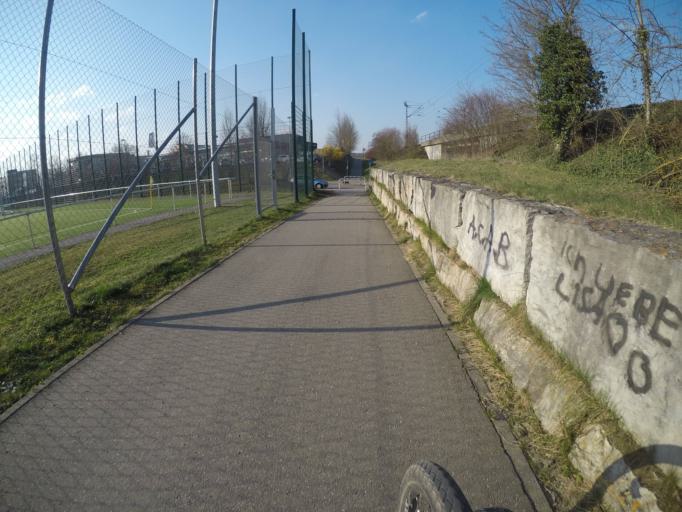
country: DE
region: Baden-Wuerttemberg
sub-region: Regierungsbezirk Stuttgart
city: Herrenberg
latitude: 48.5996
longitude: 8.8660
